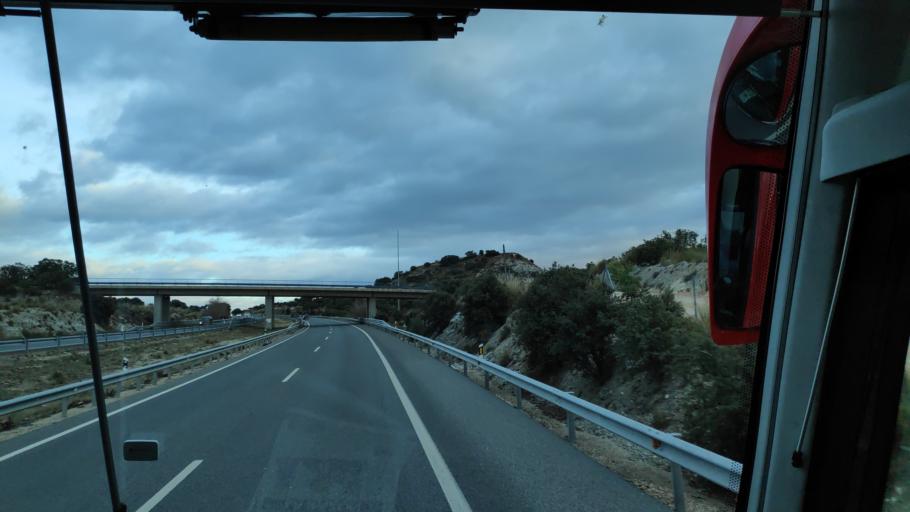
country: ES
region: Madrid
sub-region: Provincia de Madrid
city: Fuentiduena de Tajo
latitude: 40.1419
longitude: -3.2091
